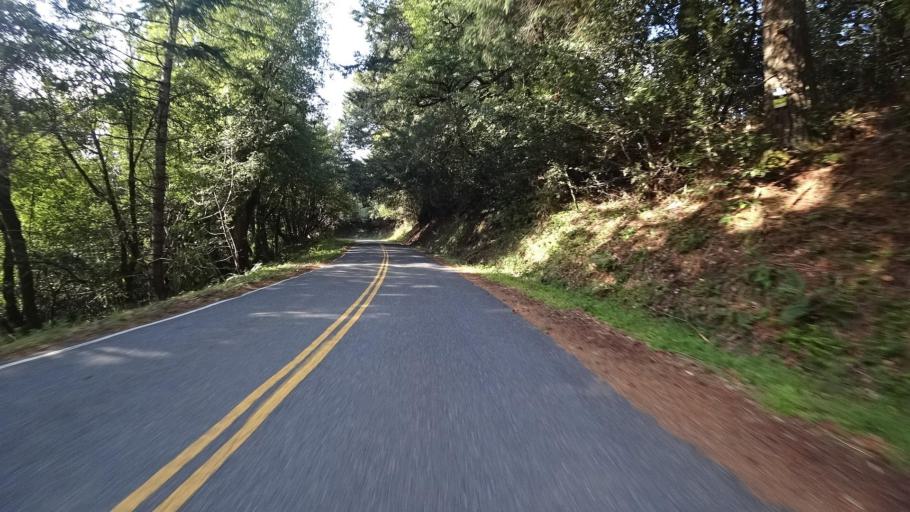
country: US
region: California
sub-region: Humboldt County
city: Blue Lake
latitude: 40.7241
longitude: -123.9445
